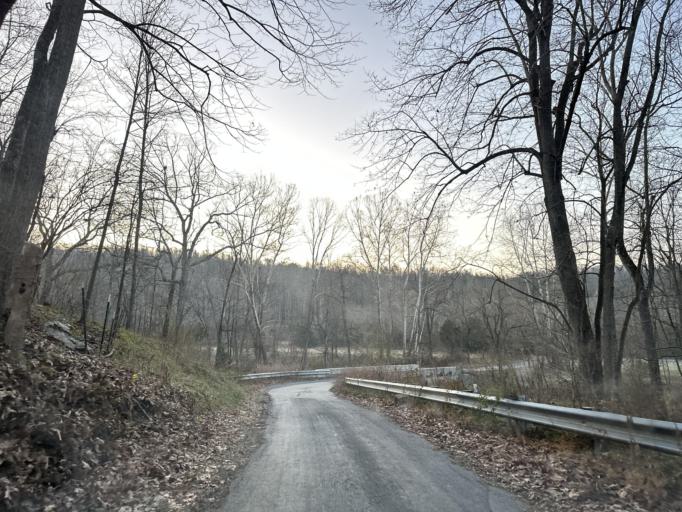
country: US
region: Virginia
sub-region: Rockbridge County
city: East Lexington
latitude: 38.0782
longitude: -79.3681
